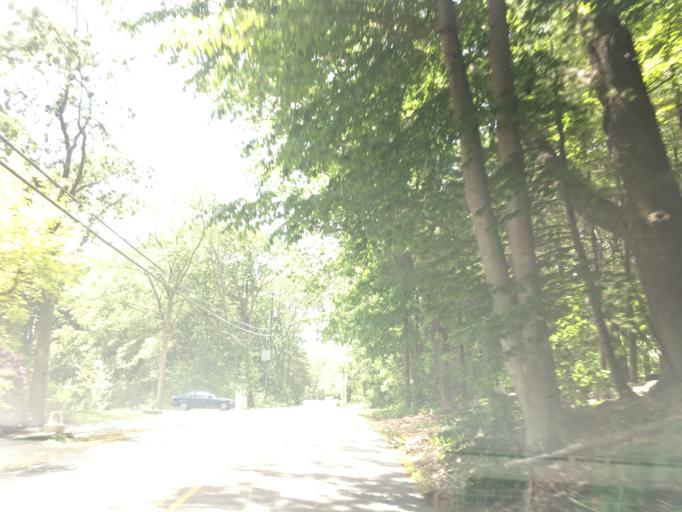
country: US
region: New Hampshire
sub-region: Rockingham County
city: Stratham Station
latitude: 43.0226
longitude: -70.8775
